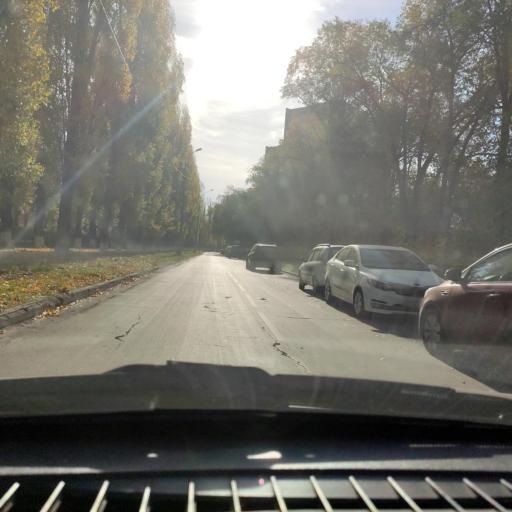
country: RU
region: Samara
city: Tol'yatti
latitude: 53.5247
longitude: 49.2680
